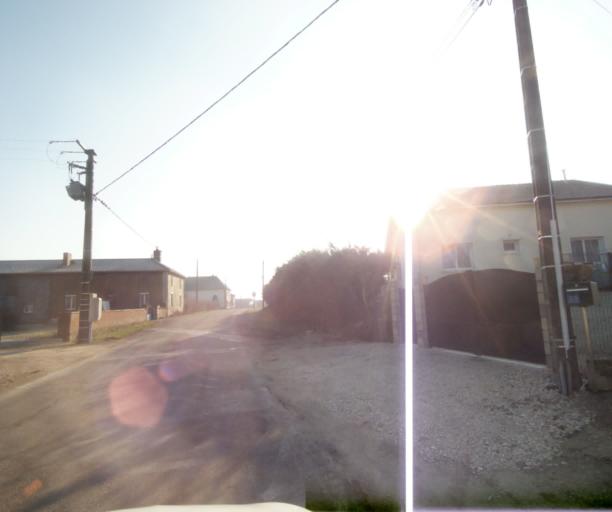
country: FR
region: Champagne-Ardenne
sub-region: Departement de la Haute-Marne
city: Montier-en-Der
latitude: 48.4822
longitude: 4.7491
